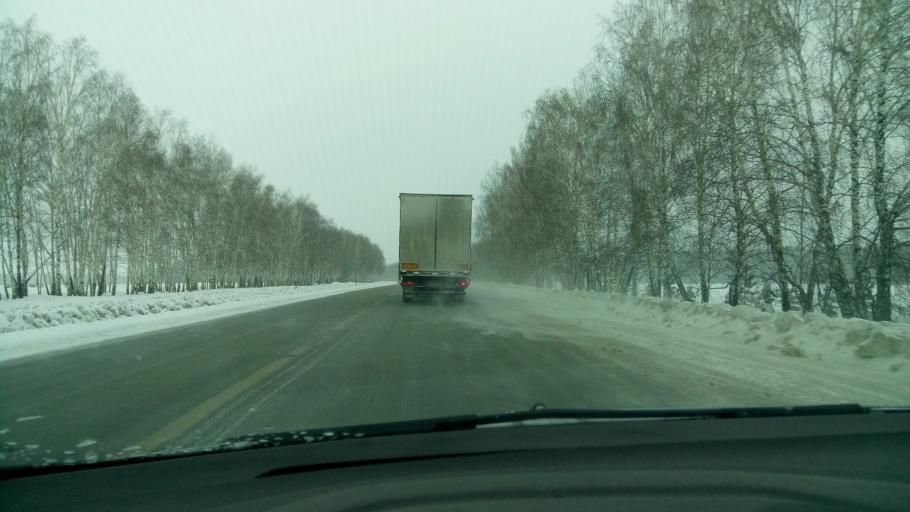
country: RU
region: Sverdlovsk
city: Zarechnyy
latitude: 56.7478
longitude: 61.3058
